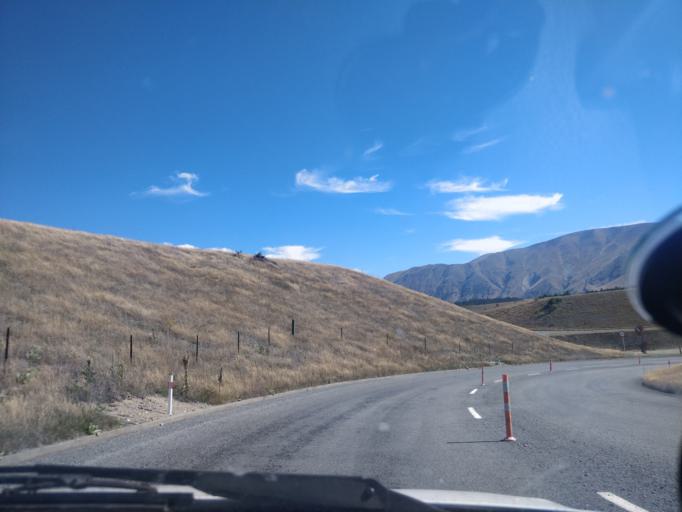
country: NZ
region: Otago
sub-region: Queenstown-Lakes District
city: Wanaka
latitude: -44.2663
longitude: 170.0337
